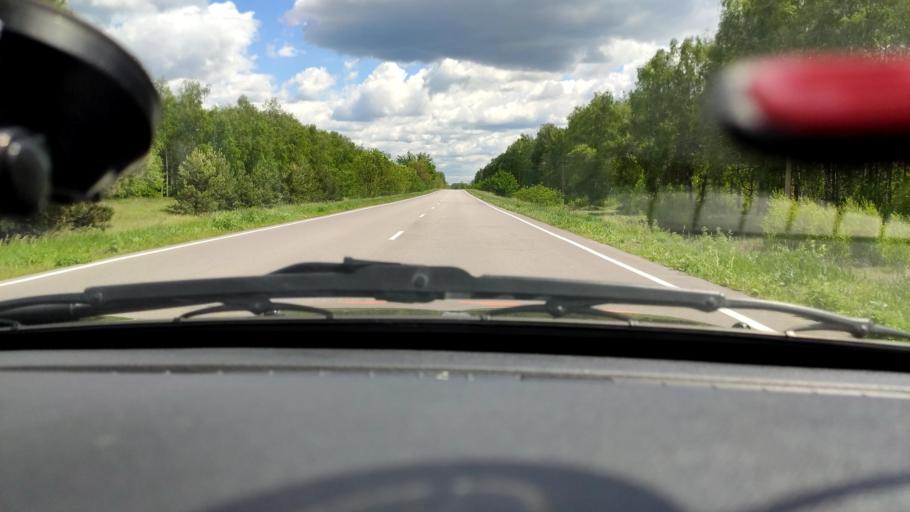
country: RU
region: Belgorod
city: Krasnoye
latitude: 51.0565
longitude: 38.8655
